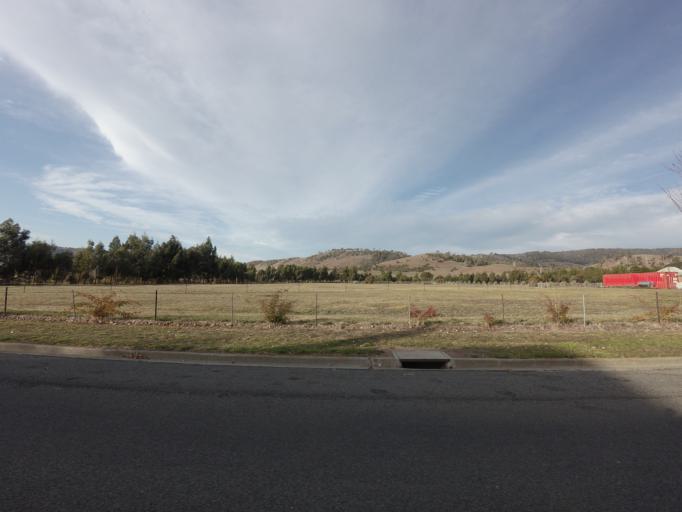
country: AU
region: Tasmania
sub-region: Brighton
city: Bridgewater
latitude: -42.5374
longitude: 147.2036
